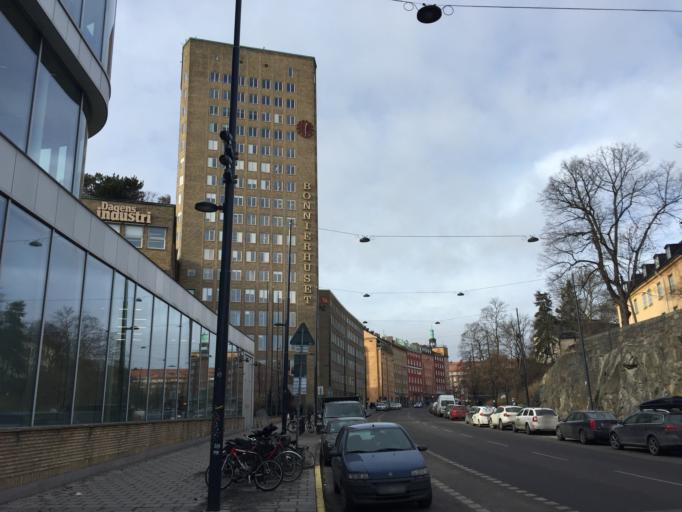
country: SE
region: Stockholm
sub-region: Stockholms Kommun
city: Stockholm
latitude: 59.3371
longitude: 18.0427
